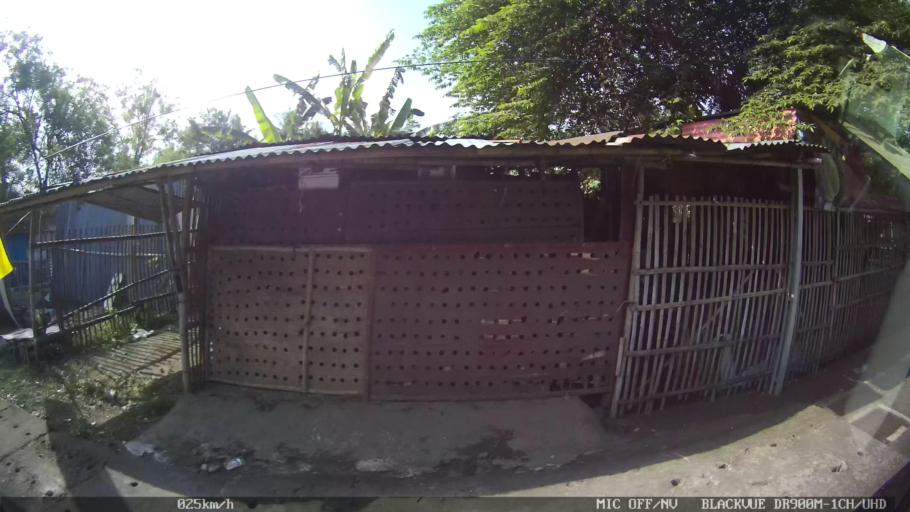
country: ID
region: Daerah Istimewa Yogyakarta
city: Depok
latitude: -7.7528
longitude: 110.4429
